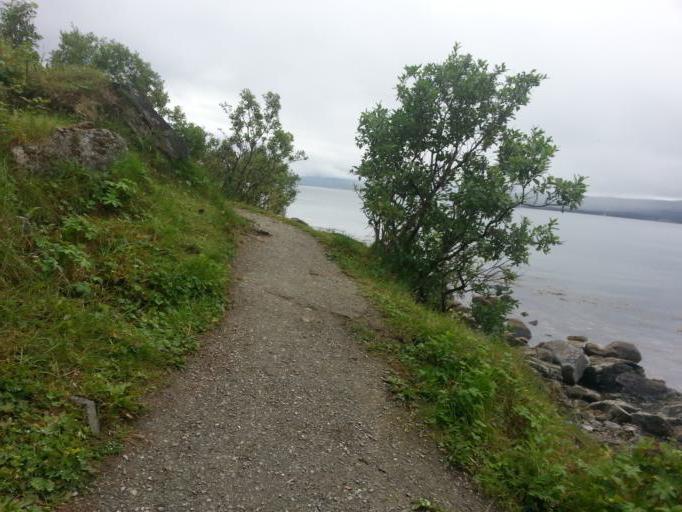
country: NO
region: Troms
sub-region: Tromso
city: Tromso
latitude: 69.6327
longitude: 18.9054
